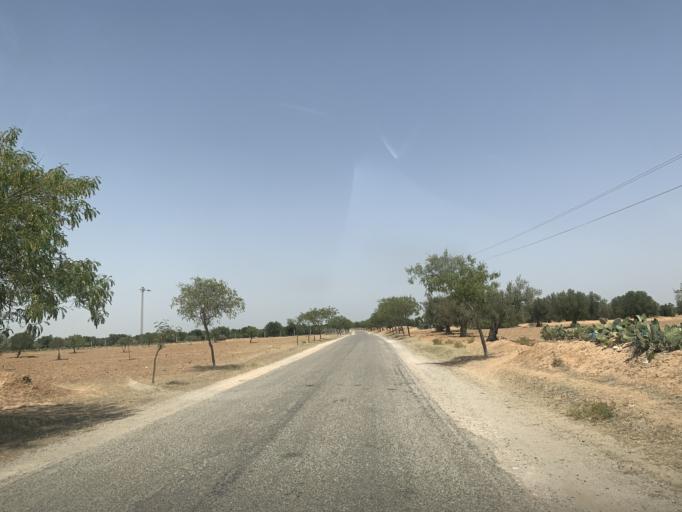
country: TN
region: Al Mahdiyah
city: Shurban
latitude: 35.1893
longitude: 10.2460
